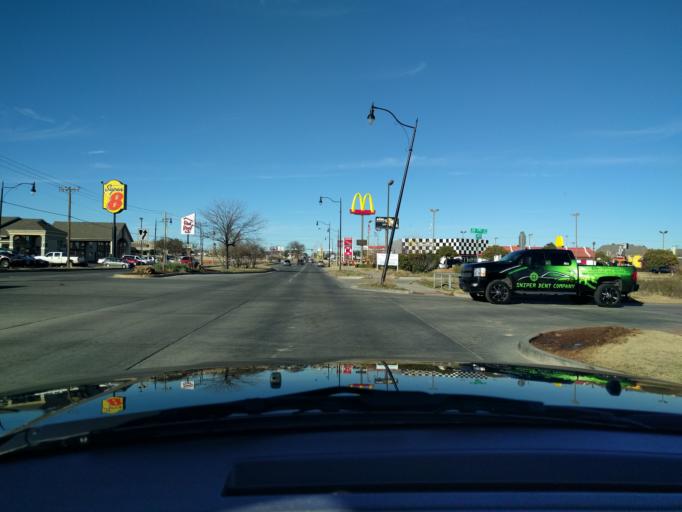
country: US
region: Oklahoma
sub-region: Oklahoma County
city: Warr Acres
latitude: 35.4622
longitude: -97.6010
